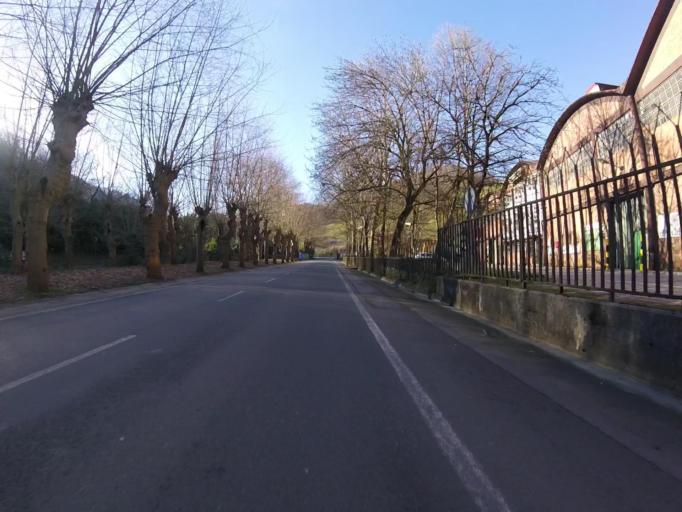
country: ES
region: Navarre
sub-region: Provincia de Navarra
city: Lesaka
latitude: 43.2474
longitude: -1.7122
